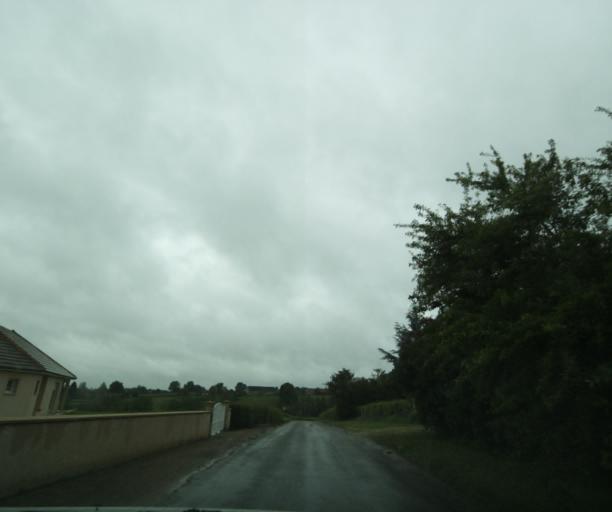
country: FR
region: Bourgogne
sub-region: Departement de Saone-et-Loire
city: Palinges
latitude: 46.5507
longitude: 4.2000
